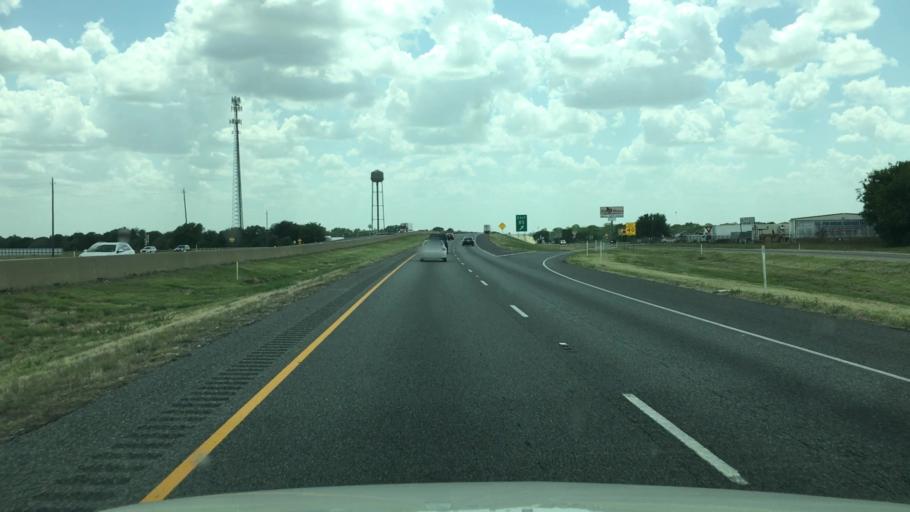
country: US
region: Texas
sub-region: Hunt County
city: Caddo Mills
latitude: 33.0211
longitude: -96.2018
